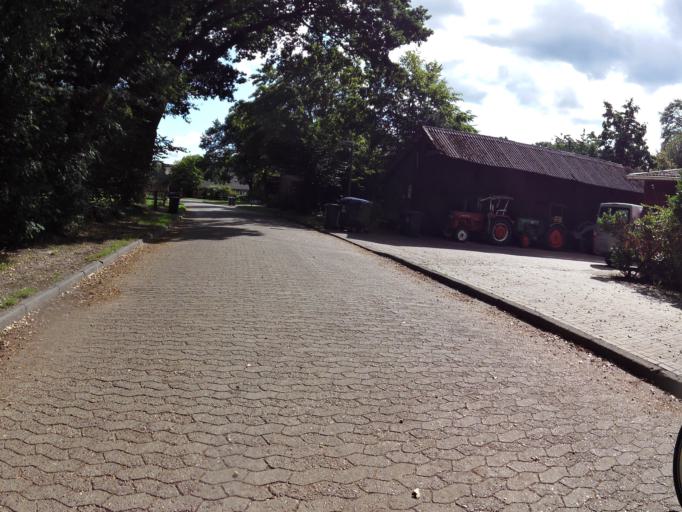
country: DE
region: Lower Saxony
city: Sandbostel
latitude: 53.3861
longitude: 9.1452
